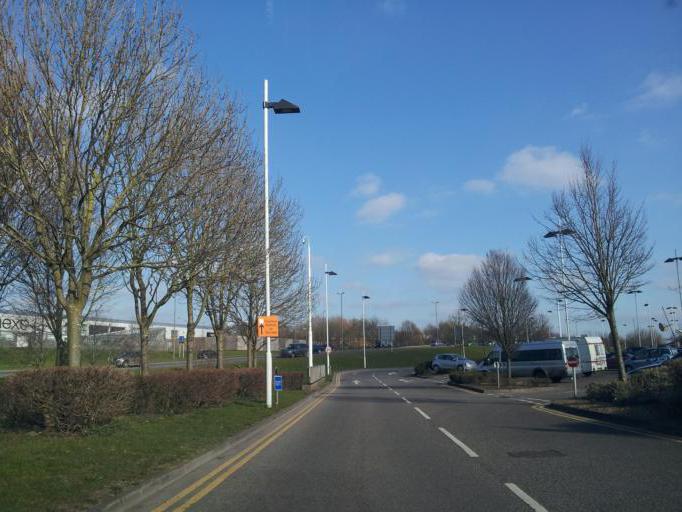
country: GB
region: England
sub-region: South Gloucestershire
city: Almondsbury
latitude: 51.5244
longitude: -2.6035
